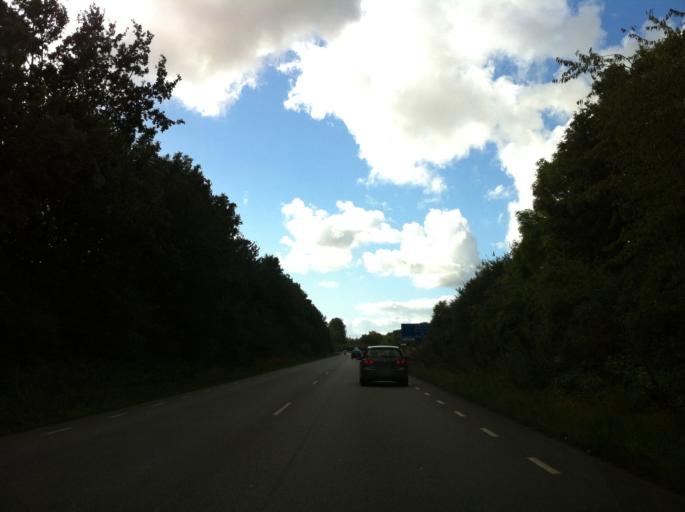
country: SE
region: Skane
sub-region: Kavlinge Kommun
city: Kaevlinge
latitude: 55.7980
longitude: 13.1382
